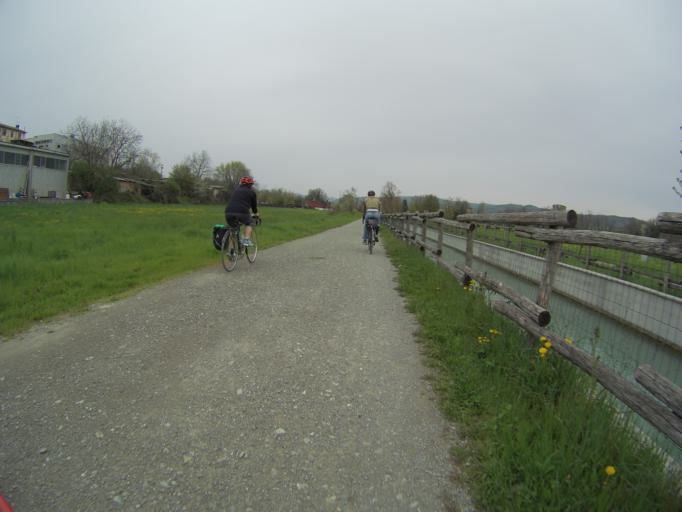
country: IT
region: Emilia-Romagna
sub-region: Provincia di Reggio Emilia
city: Ciano d'Enza
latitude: 44.6145
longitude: 10.4119
